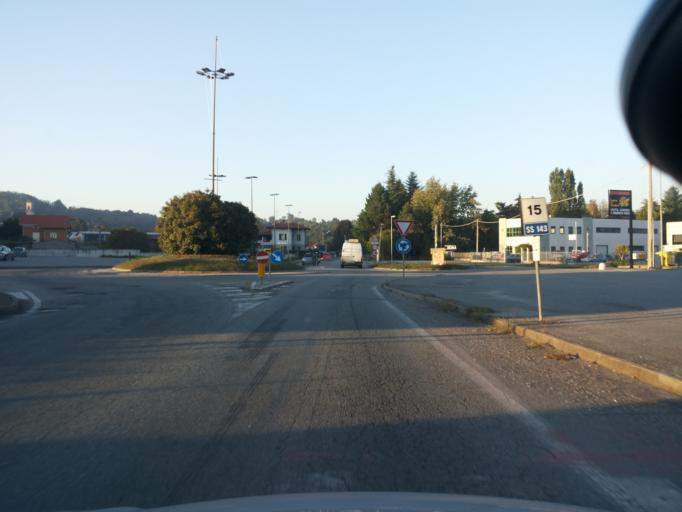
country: IT
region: Piedmont
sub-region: Provincia di Biella
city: Dorzano
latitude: 45.4206
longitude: 8.0995
